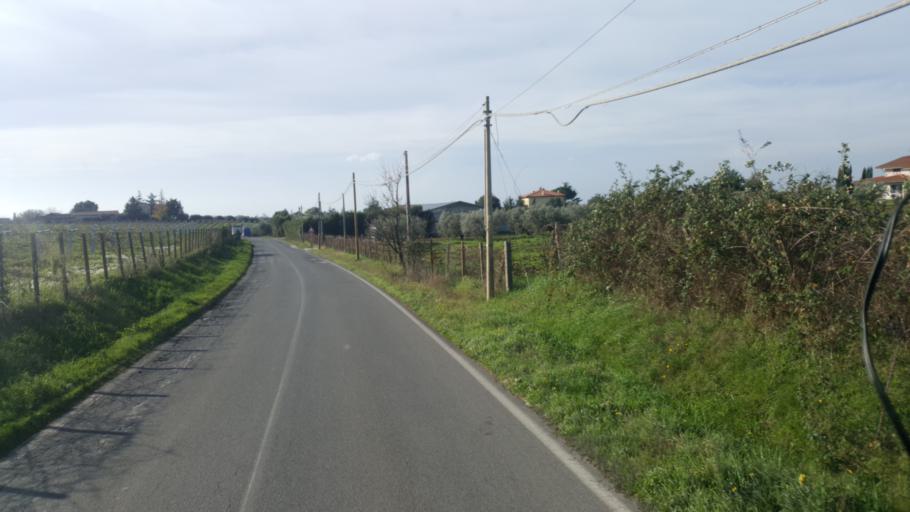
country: IT
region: Latium
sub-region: Provincia di Latina
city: Campoleone
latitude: 41.6406
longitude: 12.6171
